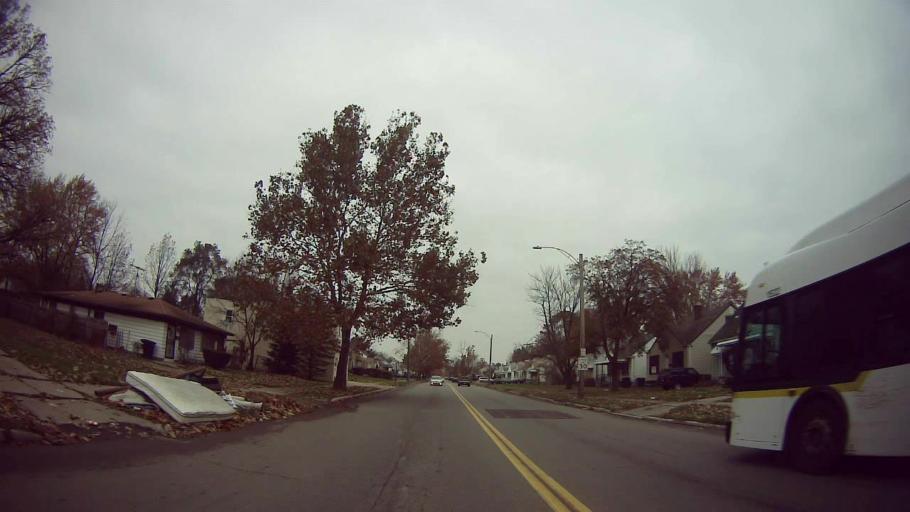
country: US
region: Michigan
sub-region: Wayne County
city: Dearborn Heights
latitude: 42.3362
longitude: -83.2351
